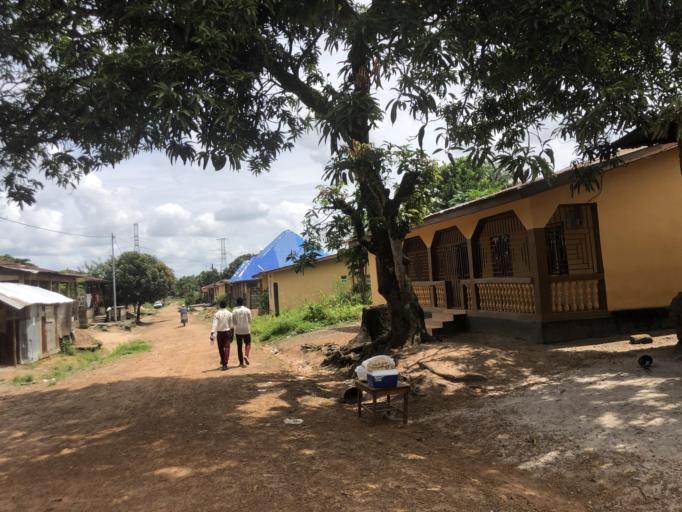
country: SL
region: Northern Province
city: Makeni
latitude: 8.8805
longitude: -12.0501
